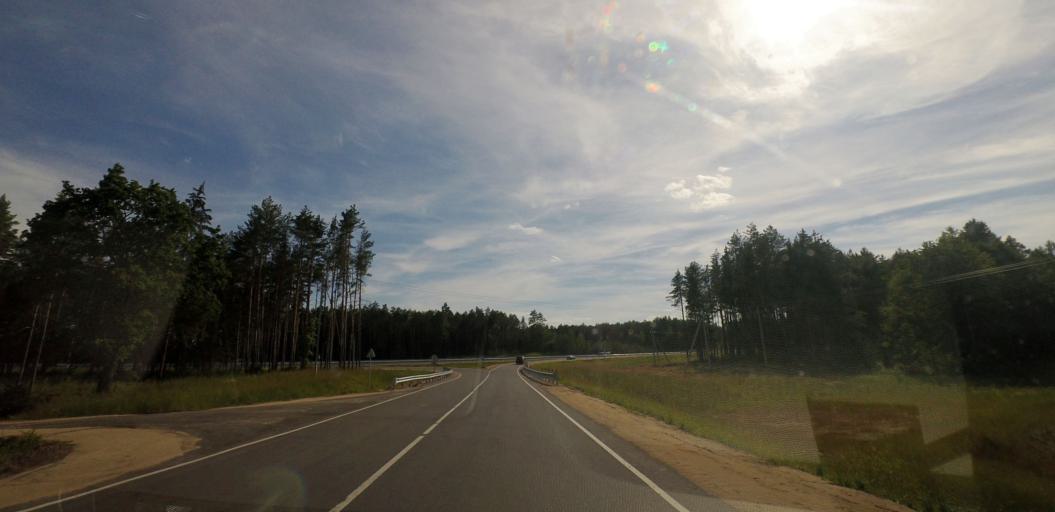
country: BY
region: Grodnenskaya
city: Iwye
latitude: 53.8837
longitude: 25.7372
